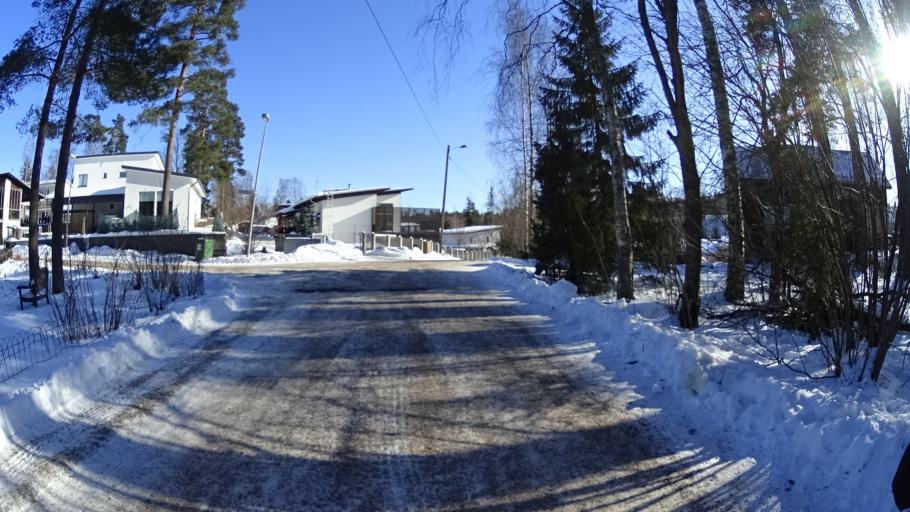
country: FI
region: Uusimaa
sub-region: Helsinki
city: Kauniainen
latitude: 60.2227
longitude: 24.6984
